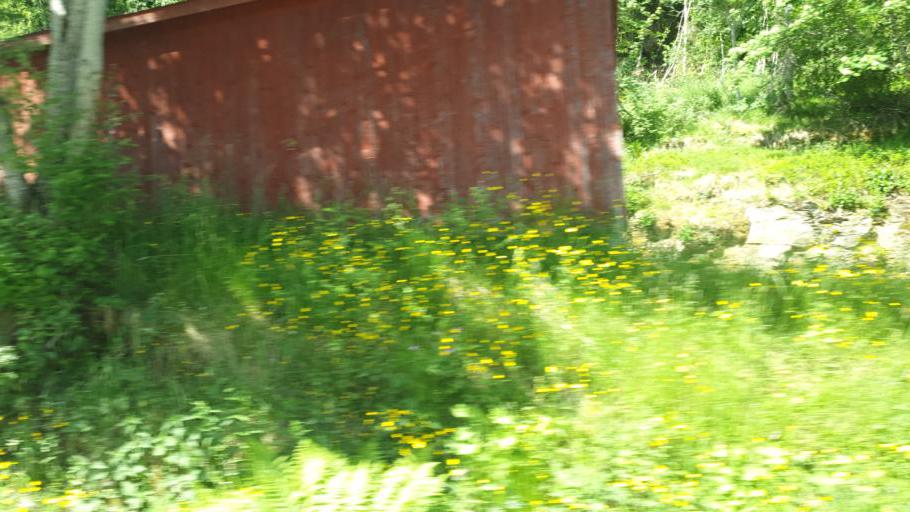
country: NO
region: Nord-Trondelag
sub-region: Leksvik
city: Leksvik
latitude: 63.6896
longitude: 10.6755
